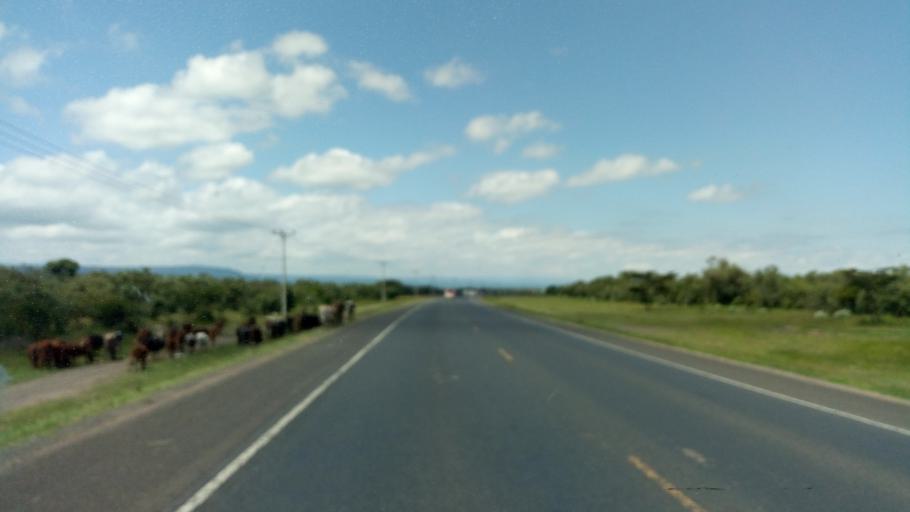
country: KE
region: Nakuru
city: Naivasha
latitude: -0.5483
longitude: 36.3459
